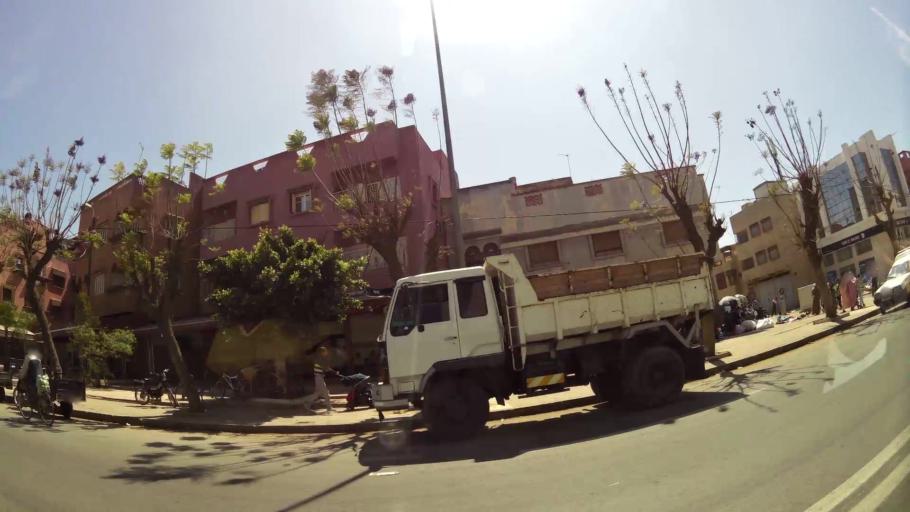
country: MA
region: Gharb-Chrarda-Beni Hssen
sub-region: Kenitra Province
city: Kenitra
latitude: 34.2422
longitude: -6.5492
